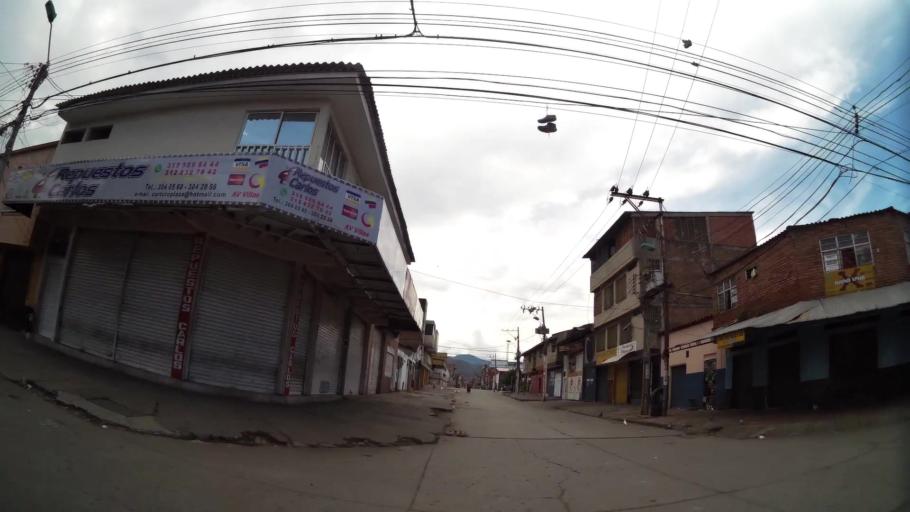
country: CO
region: Valle del Cauca
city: Cali
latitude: 3.4428
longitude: -76.5224
